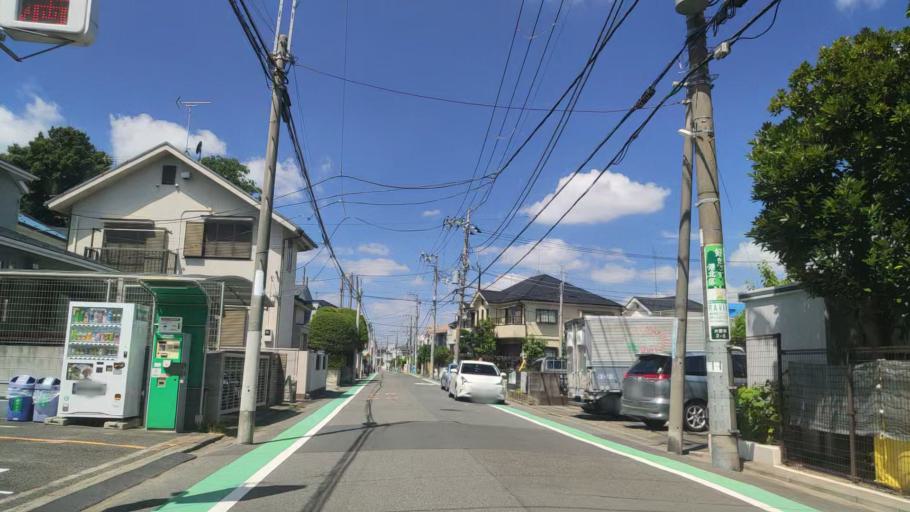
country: JP
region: Kanagawa
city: Yokohama
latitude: 35.5272
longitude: 139.6304
